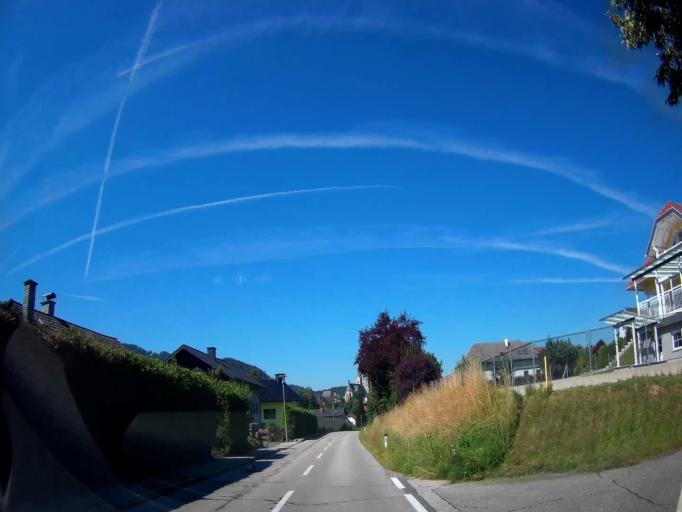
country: AT
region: Carinthia
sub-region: Politischer Bezirk Klagenfurt Land
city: Maria Saal
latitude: 46.6845
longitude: 14.3524
